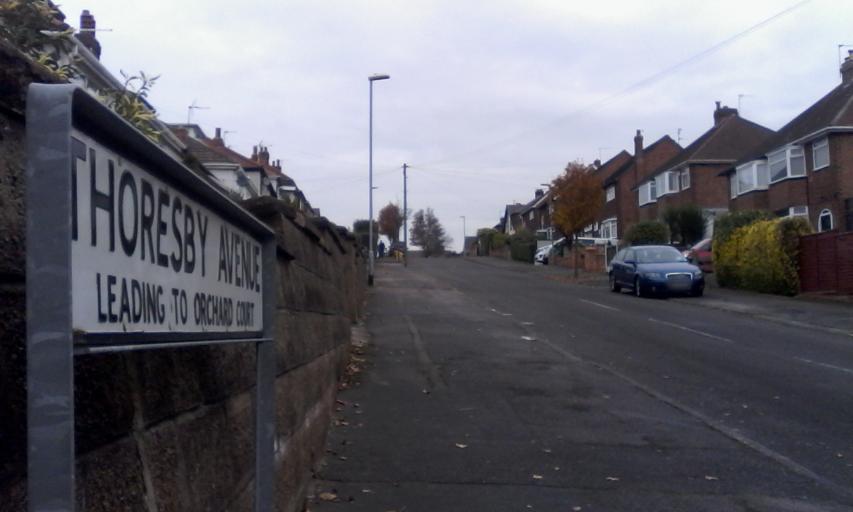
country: GB
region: England
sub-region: Nottinghamshire
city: Arnold
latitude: 52.9780
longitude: -1.0949
